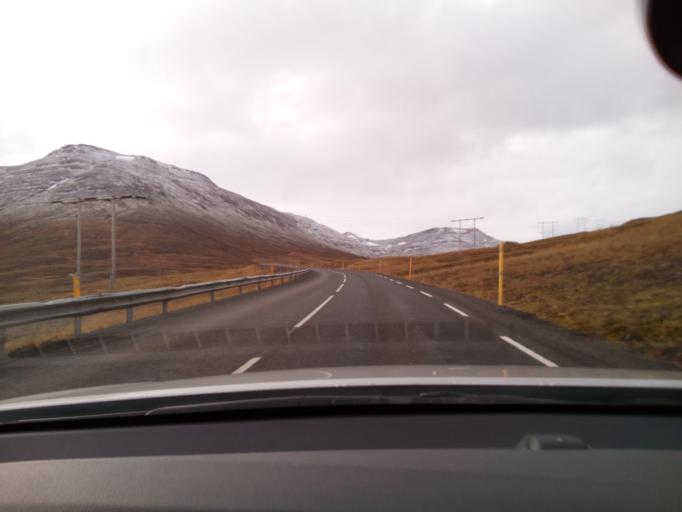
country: IS
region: Northeast
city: Dalvik
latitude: 65.4754
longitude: -18.6672
